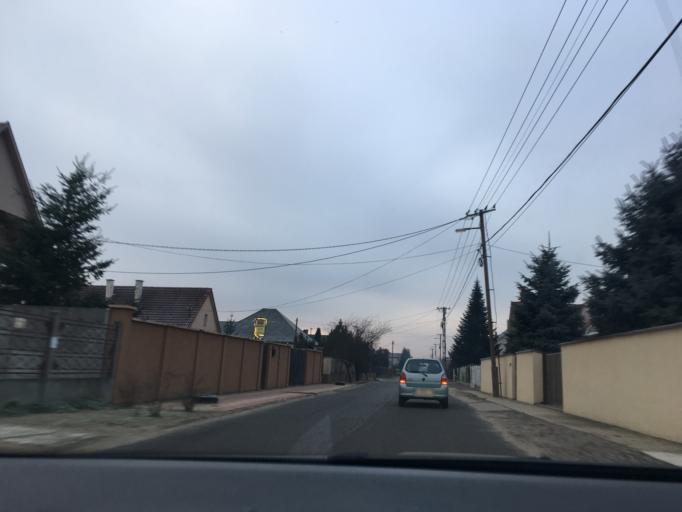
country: HU
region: Hajdu-Bihar
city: Debrecen
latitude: 47.5454
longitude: 21.6661
